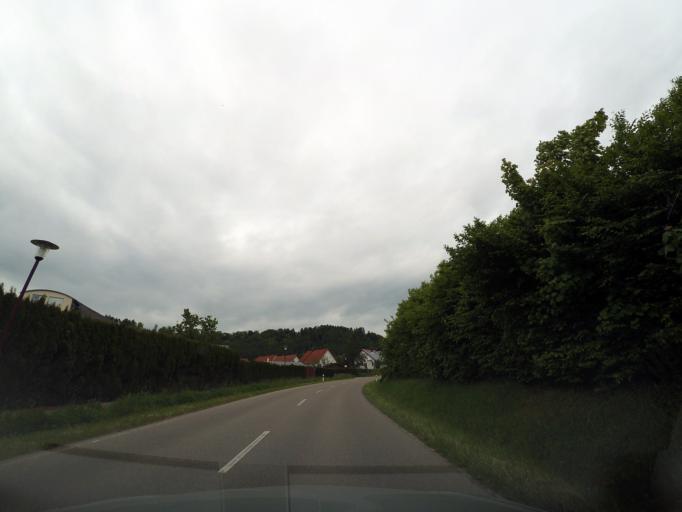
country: DE
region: Baden-Wuerttemberg
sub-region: Regierungsbezirk Stuttgart
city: Oberrot
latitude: 49.0159
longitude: 9.6711
